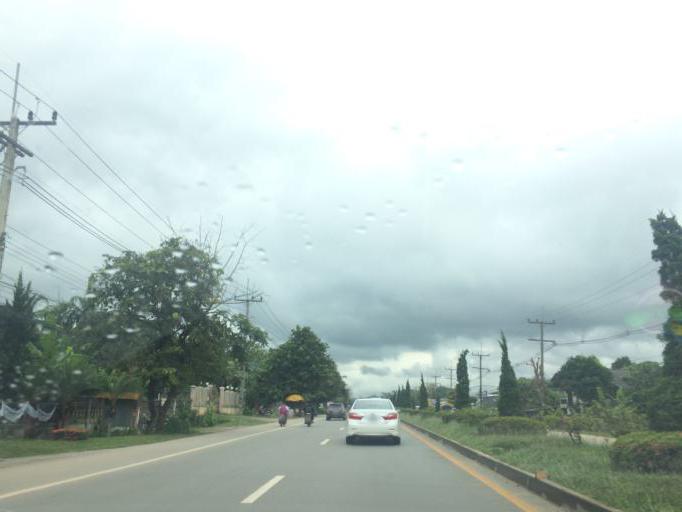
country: TH
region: Chiang Rai
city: Chiang Rai
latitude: 20.0249
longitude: 99.8722
